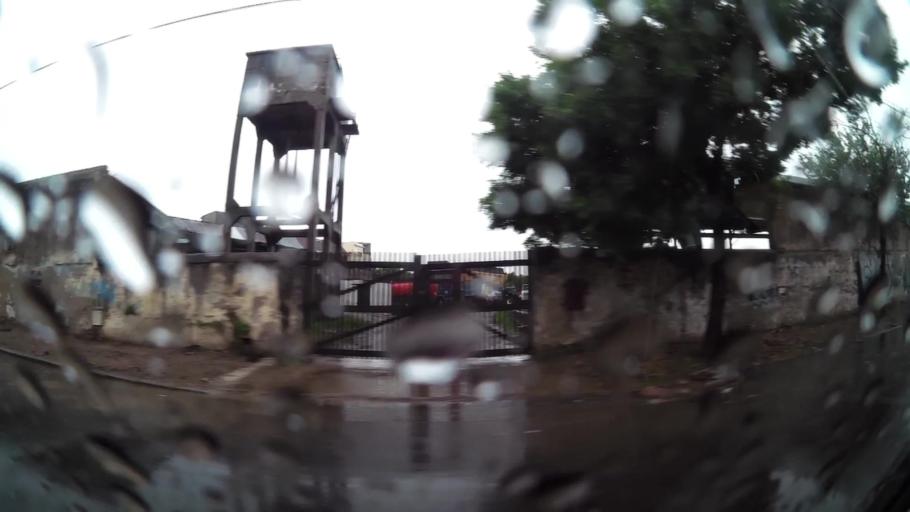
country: AR
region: Buenos Aires
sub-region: Partido de Avellaneda
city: Avellaneda
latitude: -34.6482
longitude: -58.4071
